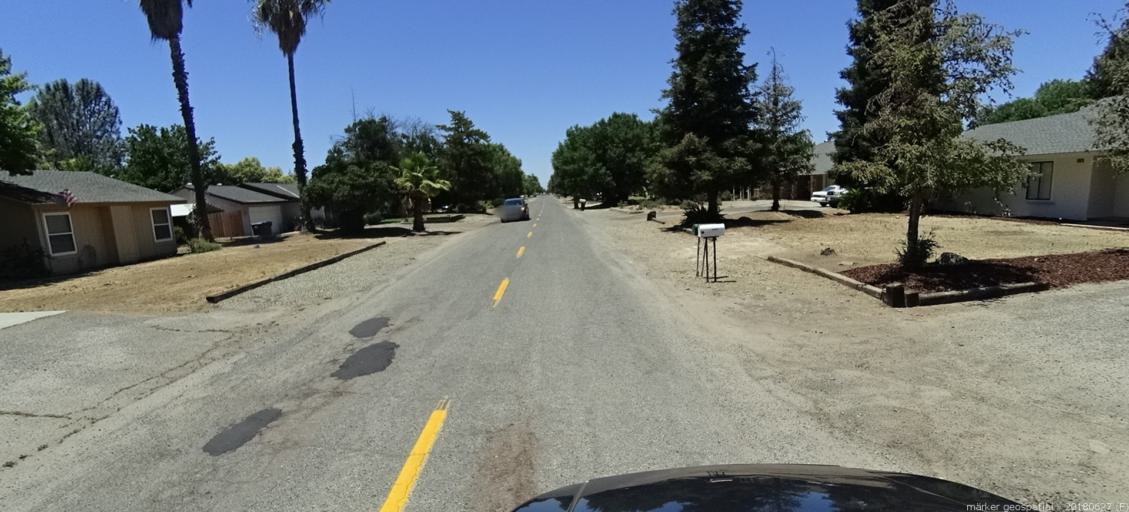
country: US
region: California
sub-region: Madera County
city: Bonadelle Ranchos-Madera Ranchos
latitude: 36.9240
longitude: -119.8789
